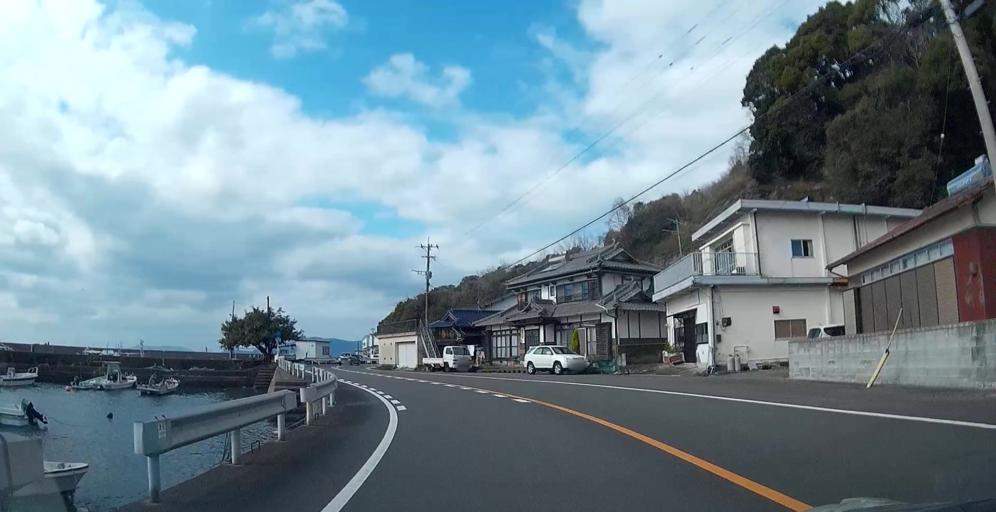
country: JP
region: Kumamoto
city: Minamata
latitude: 32.3116
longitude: 130.4719
